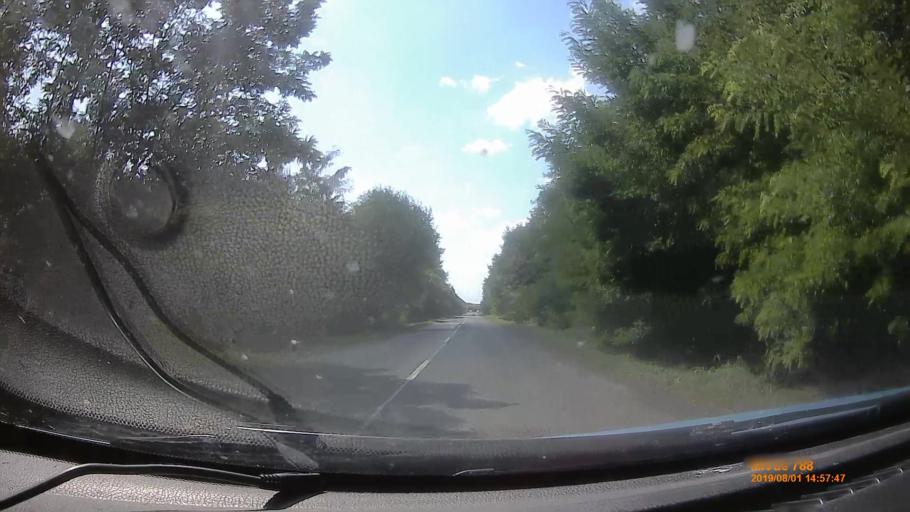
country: HU
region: Baranya
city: Vajszlo
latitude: 45.8805
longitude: 17.9254
